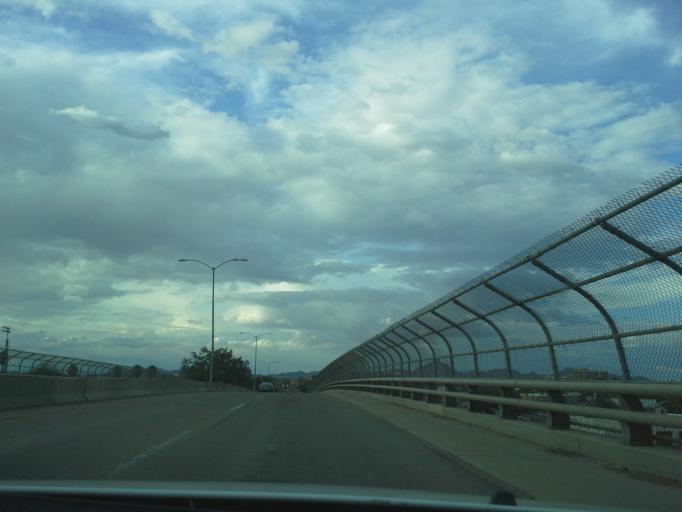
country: US
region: Arizona
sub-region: Maricopa County
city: Phoenix
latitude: 33.4442
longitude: -112.0477
